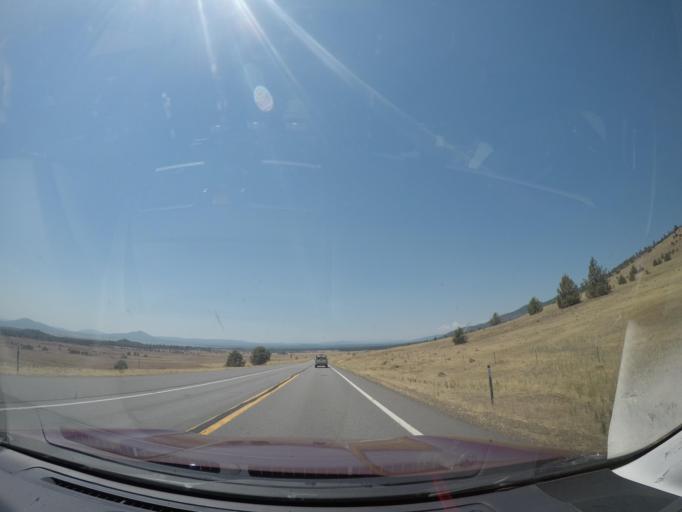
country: US
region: California
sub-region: Shasta County
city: Burney
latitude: 41.0951
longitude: -121.2800
